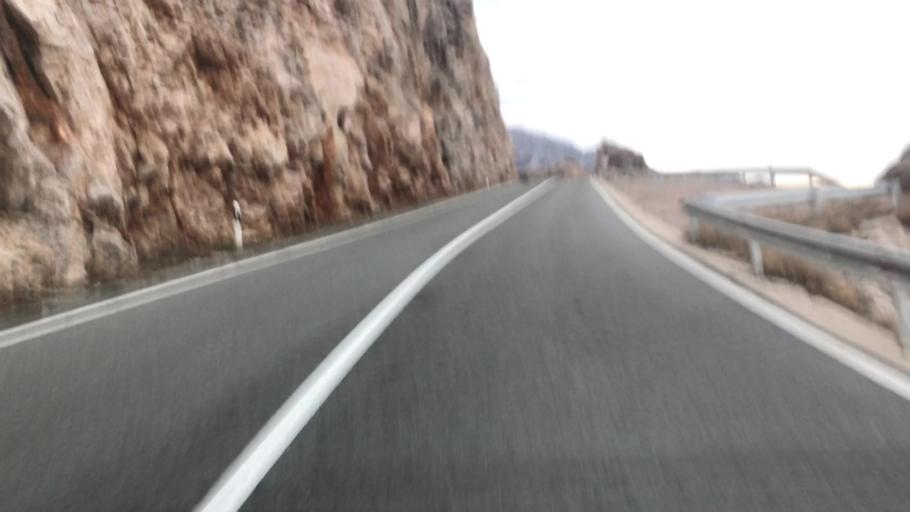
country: HR
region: Licko-Senjska
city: Karlobag
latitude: 44.5176
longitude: 15.0887
